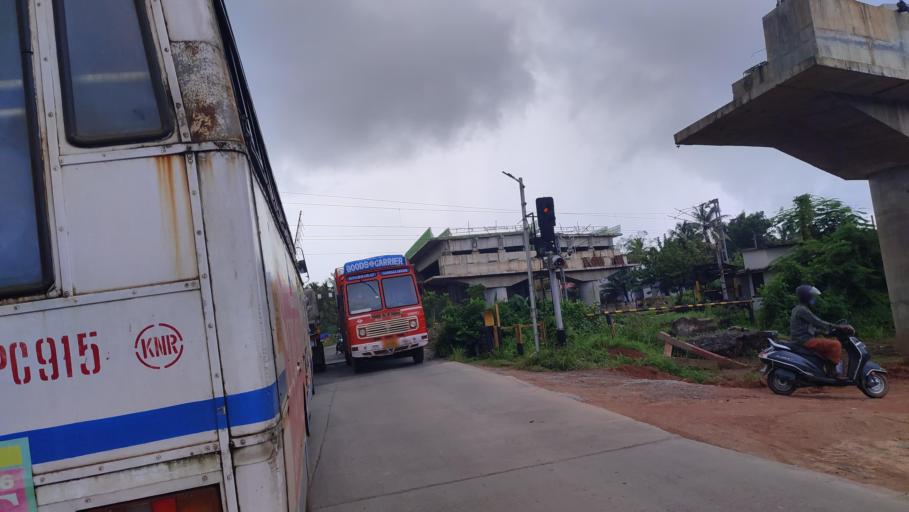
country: IN
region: Kerala
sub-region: Kasaragod District
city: Nileshwar
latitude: 12.2428
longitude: 75.1458
